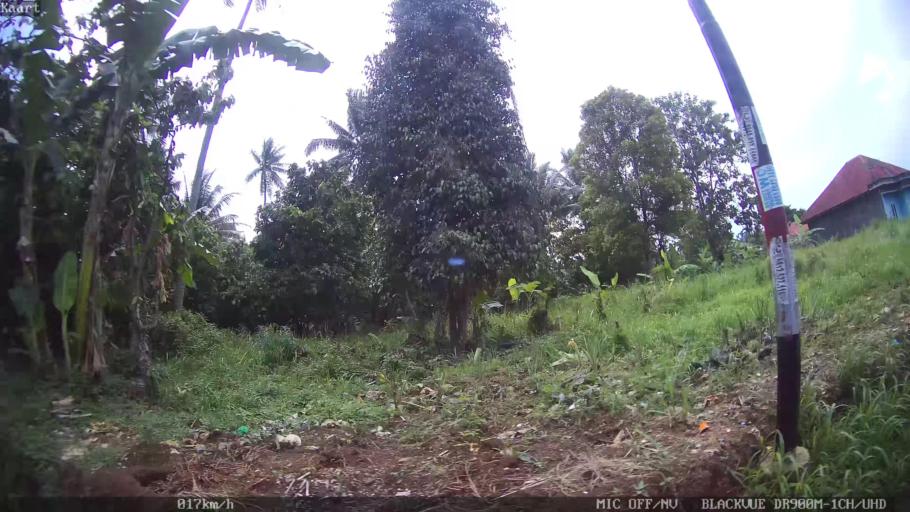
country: ID
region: Lampung
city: Kedaton
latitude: -5.3900
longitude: 105.2120
